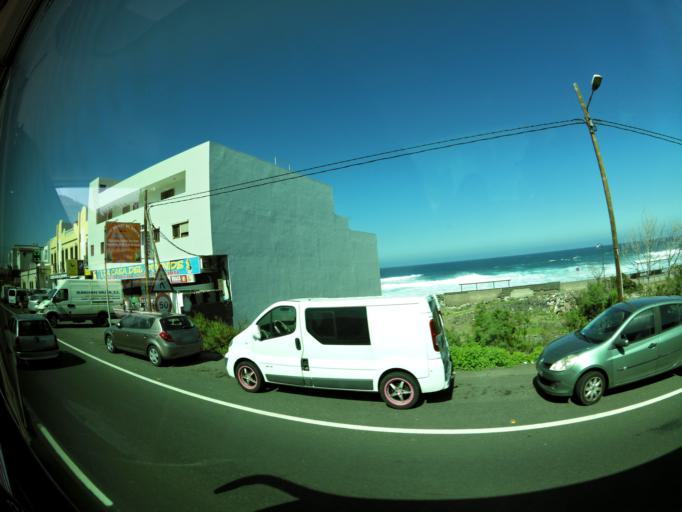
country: ES
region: Canary Islands
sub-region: Provincia de Las Palmas
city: Firgas
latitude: 28.1453
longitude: -15.5554
